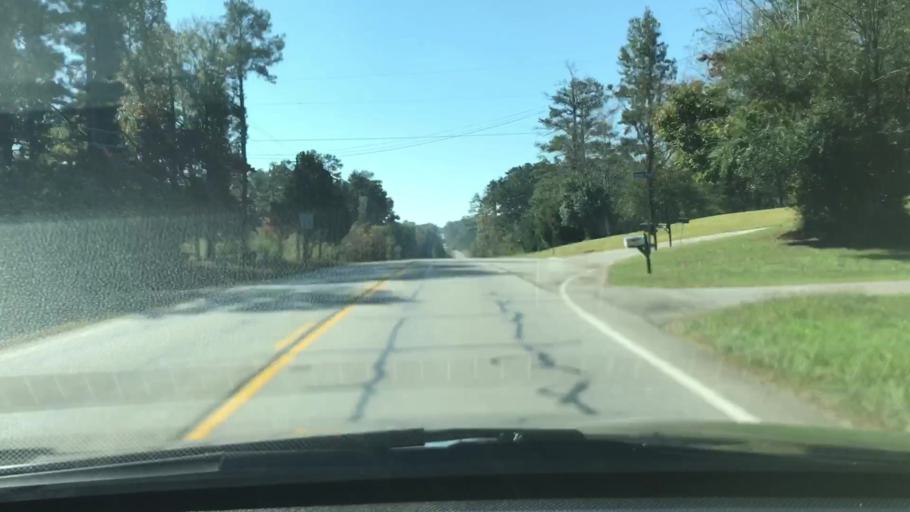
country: US
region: Georgia
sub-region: Carroll County
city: Villa Rica
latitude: 33.7859
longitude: -84.8956
